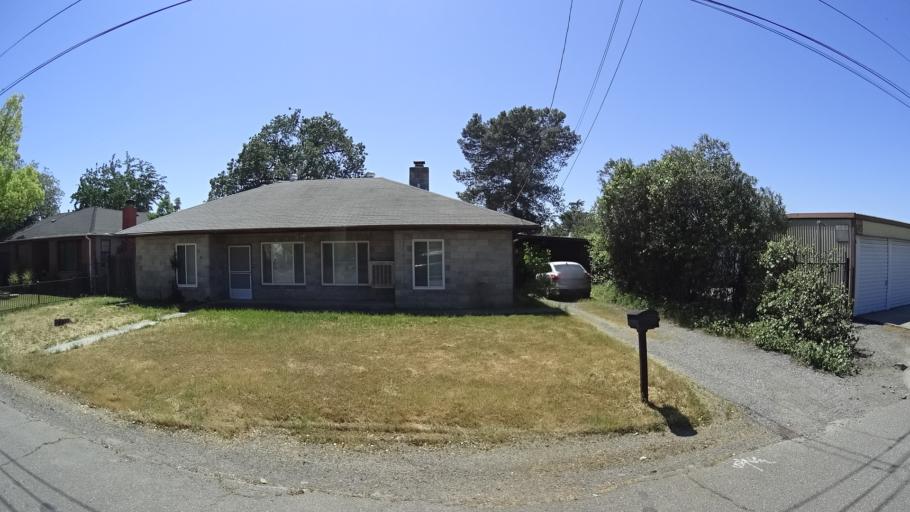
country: US
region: California
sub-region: Glenn County
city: Orland
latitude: 39.7482
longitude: -122.1796
